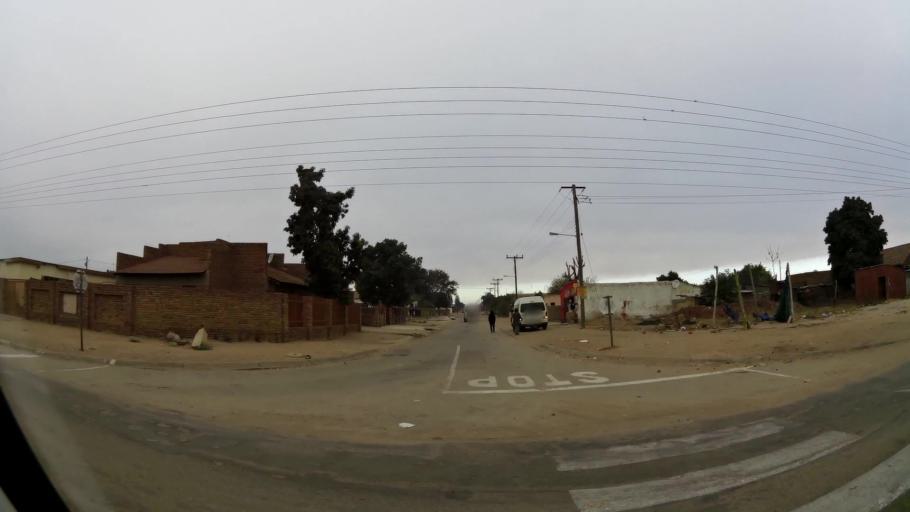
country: ZA
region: Limpopo
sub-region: Capricorn District Municipality
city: Polokwane
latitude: -23.8332
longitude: 29.3839
